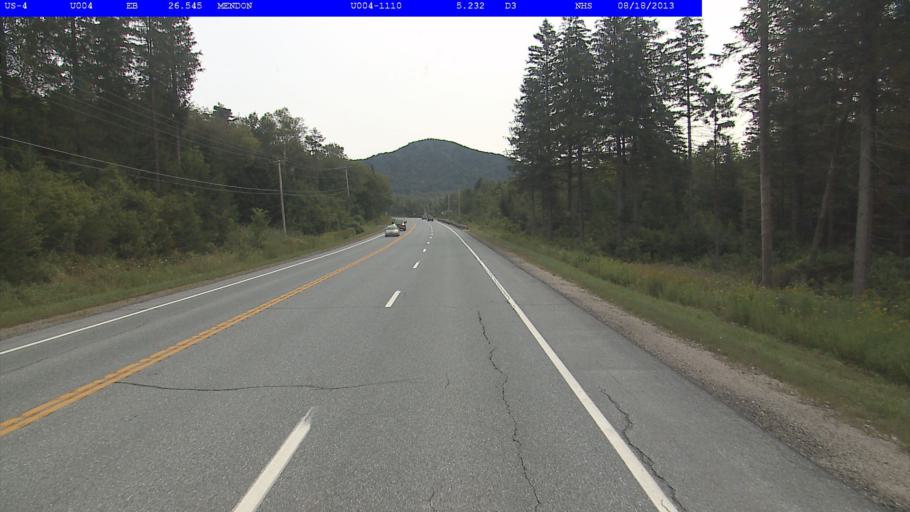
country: US
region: Vermont
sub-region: Rutland County
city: Rutland
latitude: 43.6666
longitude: -72.8593
